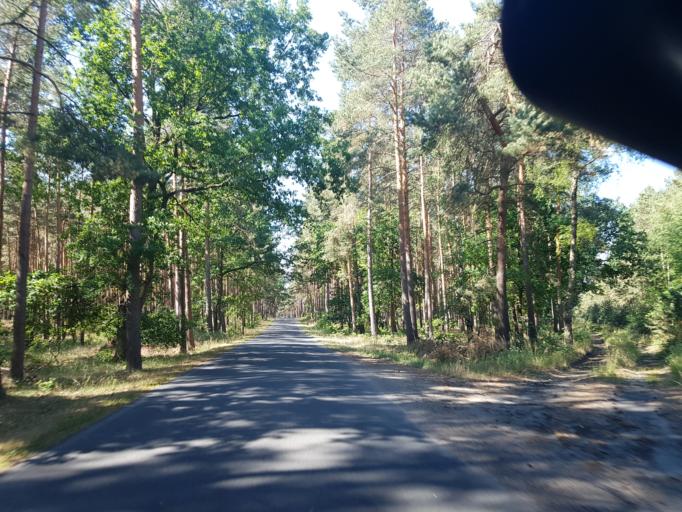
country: DE
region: Brandenburg
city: Treuenbrietzen
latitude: 52.0543
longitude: 12.8764
